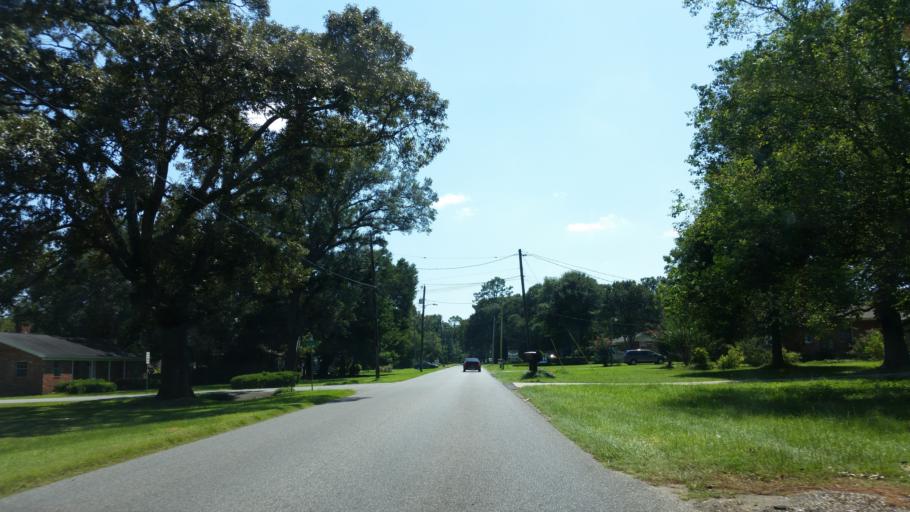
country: US
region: Florida
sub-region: Escambia County
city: Ensley
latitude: 30.5284
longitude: -87.2626
